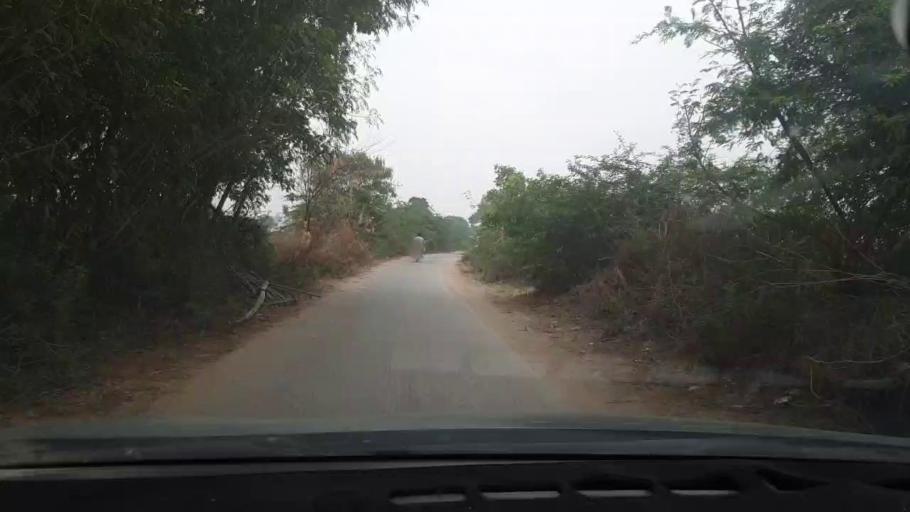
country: PK
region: Sindh
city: Malir Cantonment
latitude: 24.9241
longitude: 67.3200
